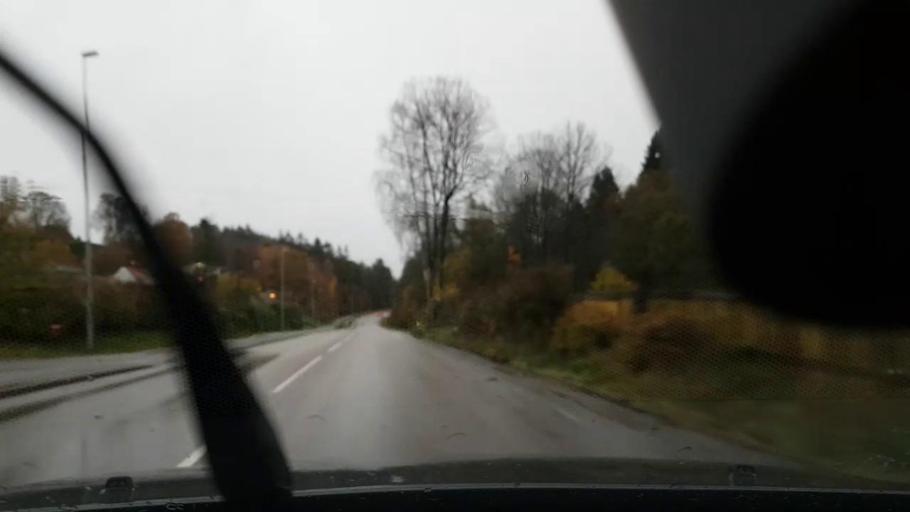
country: SE
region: Vaestra Goetaland
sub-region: Molndal
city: Kallered
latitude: 57.6020
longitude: 12.0799
